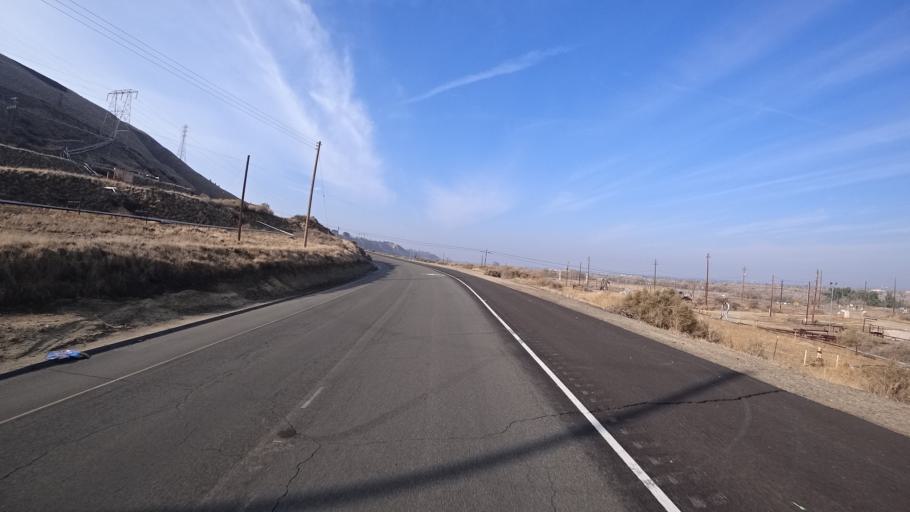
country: US
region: California
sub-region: Kern County
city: Oildale
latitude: 35.4164
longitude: -118.9660
